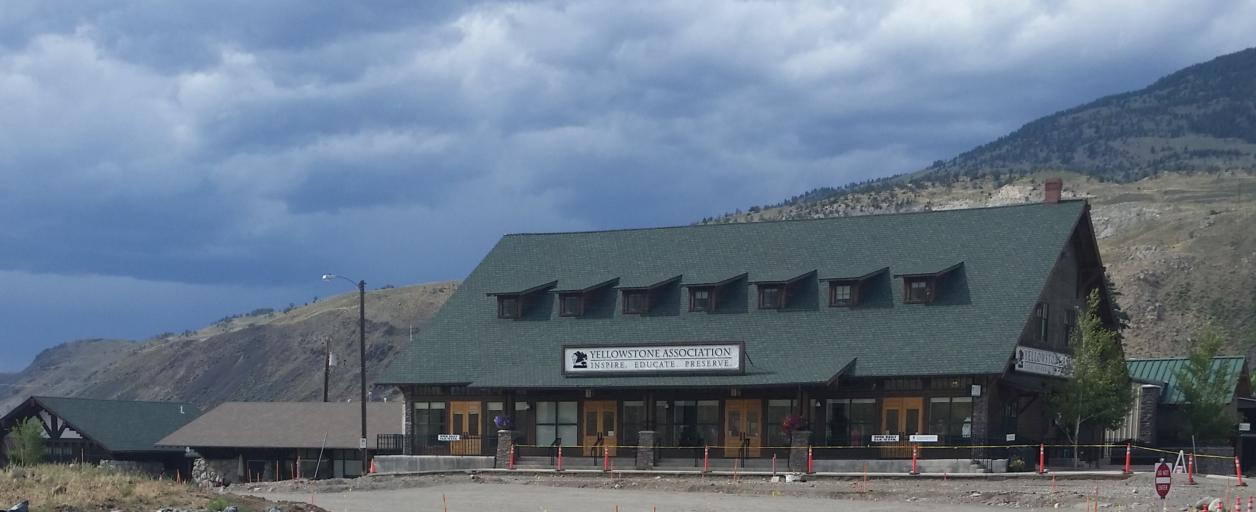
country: US
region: Montana
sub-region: Gallatin County
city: West Yellowstone
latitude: 45.0289
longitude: -110.7072
